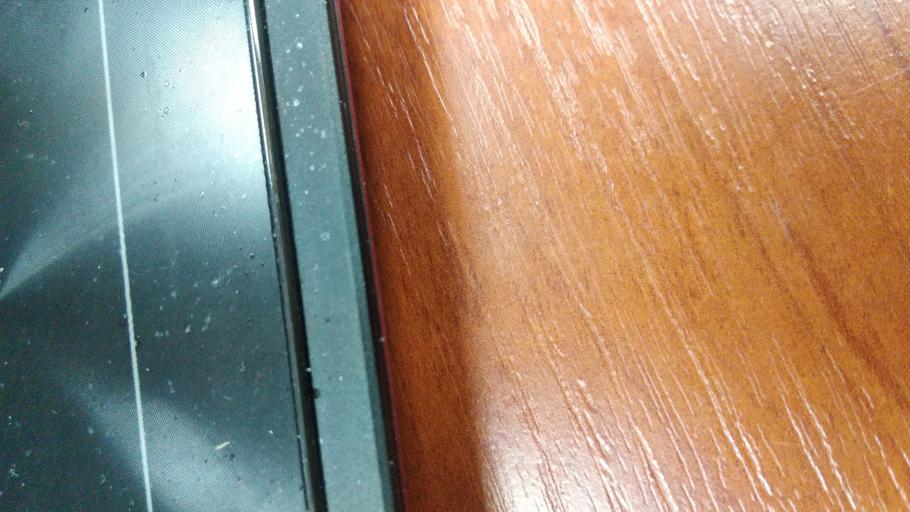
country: RU
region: Jaroslavl
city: Danilov
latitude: 58.1284
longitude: 40.4709
